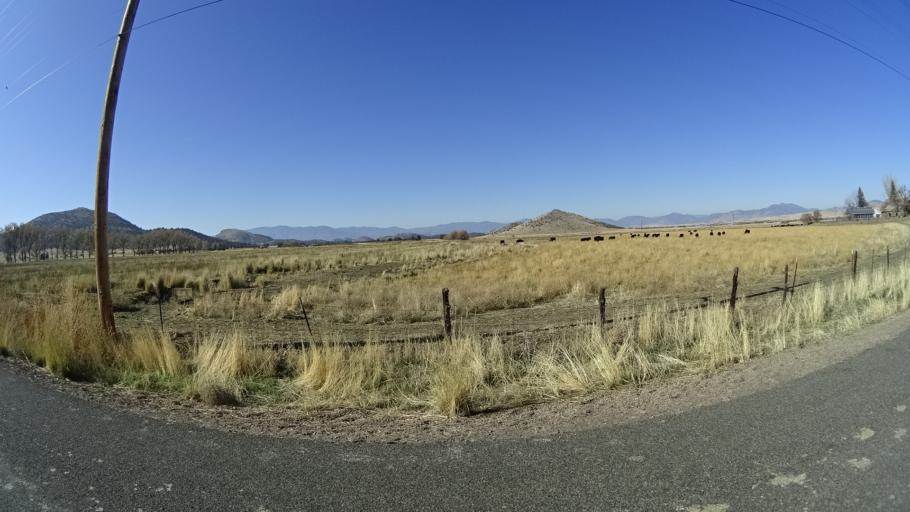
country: US
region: California
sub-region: Siskiyou County
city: Montague
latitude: 41.6876
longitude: -122.3697
